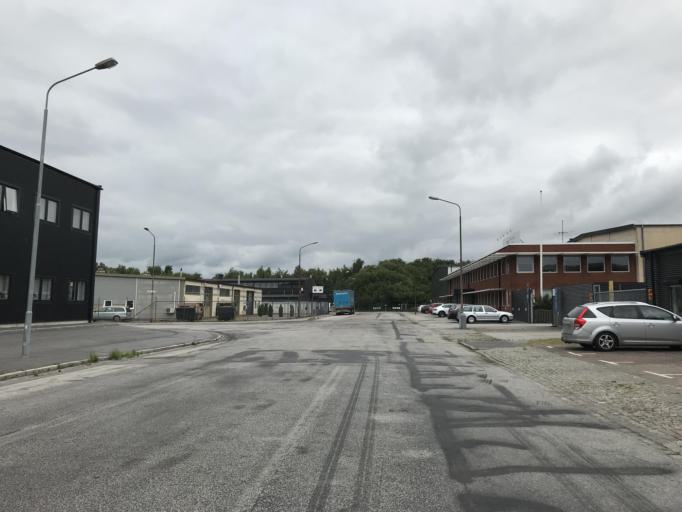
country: SE
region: Skane
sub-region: Burlovs Kommun
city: Arloev
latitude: 55.6311
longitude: 13.0598
